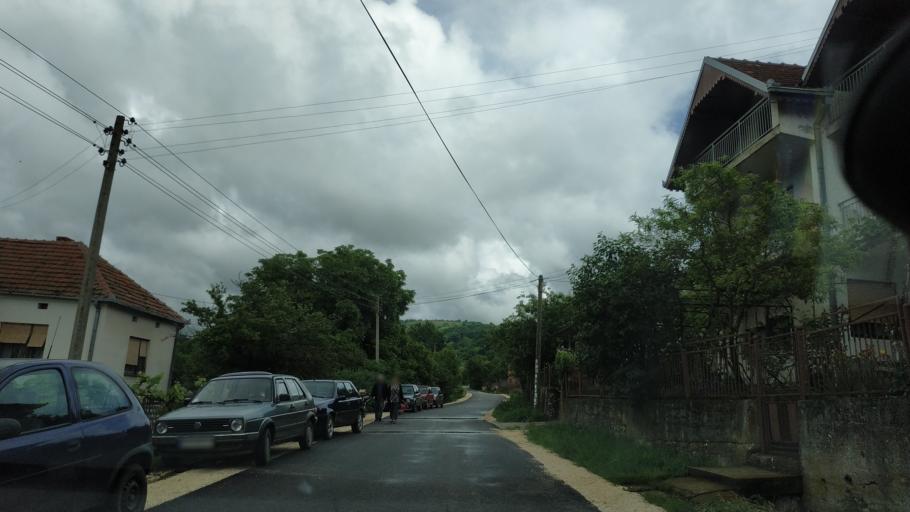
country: RS
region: Central Serbia
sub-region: Zajecarski Okrug
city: Soko Banja
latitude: 43.6754
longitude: 21.9141
